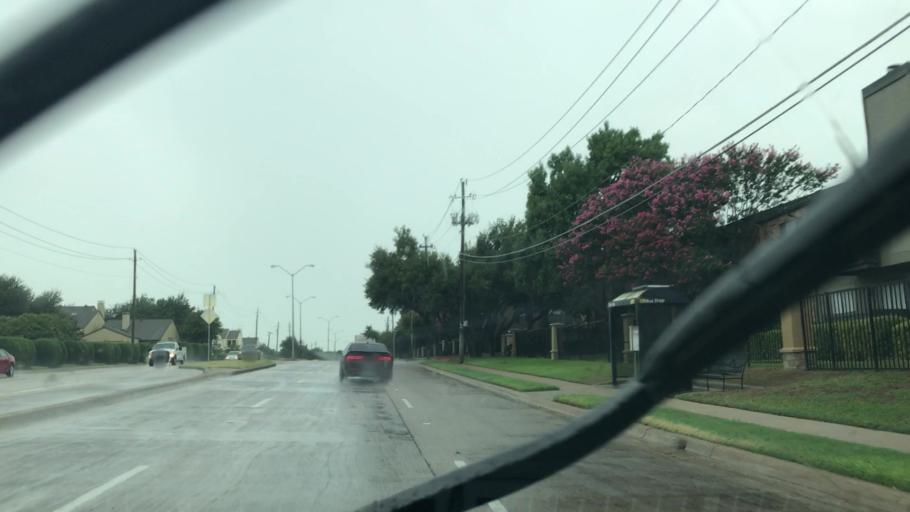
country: US
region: Texas
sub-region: Dallas County
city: Addison
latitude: 32.9388
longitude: -96.8042
